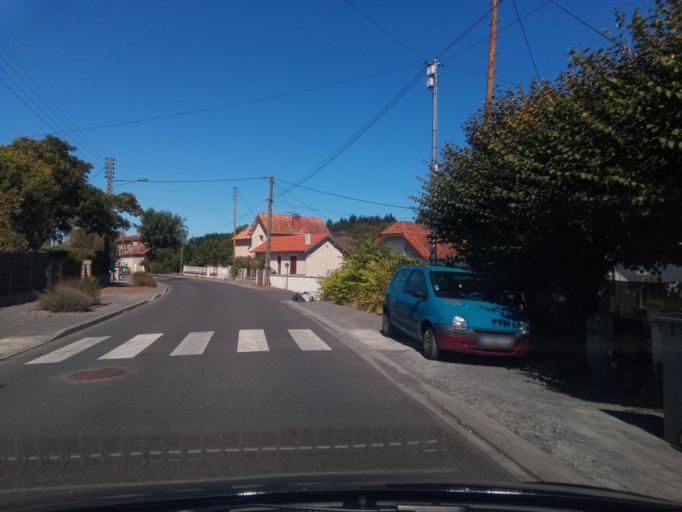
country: FR
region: Poitou-Charentes
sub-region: Departement de la Vienne
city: Montmorillon
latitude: 46.4124
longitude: 0.8807
